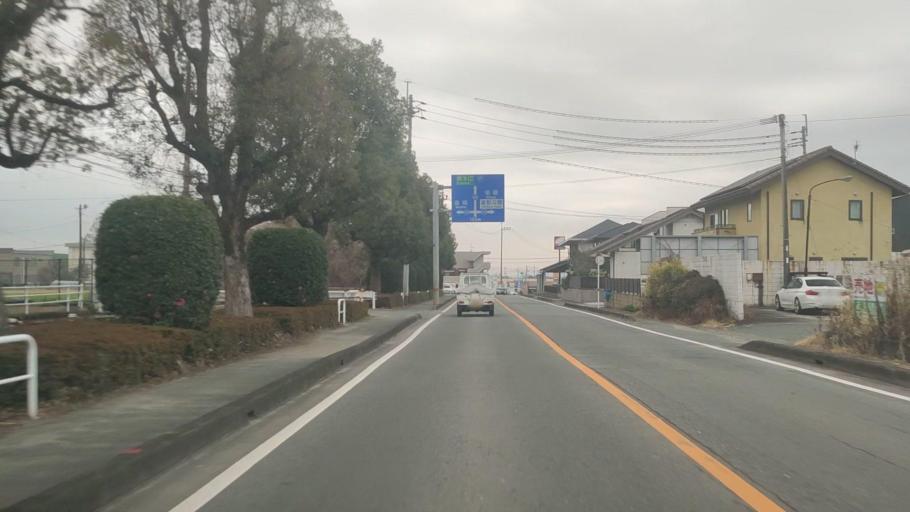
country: JP
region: Kumamoto
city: Ozu
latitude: 32.8261
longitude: 130.7961
